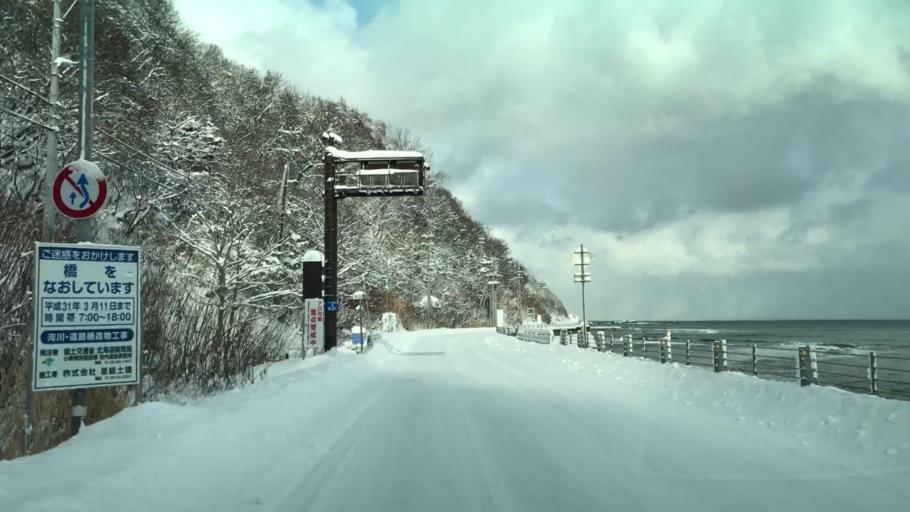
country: JP
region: Hokkaido
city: Yoichi
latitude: 43.2861
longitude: 140.6343
